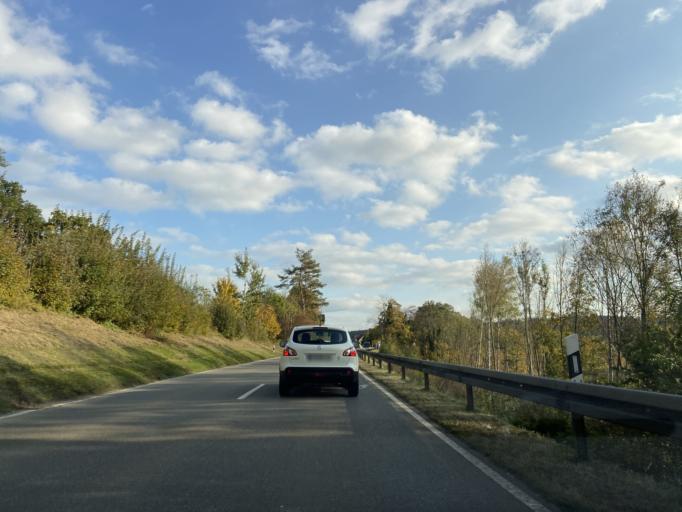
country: DE
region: Baden-Wuerttemberg
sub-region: Tuebingen Region
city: Sigmaringendorf
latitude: 48.0708
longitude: 9.2581
